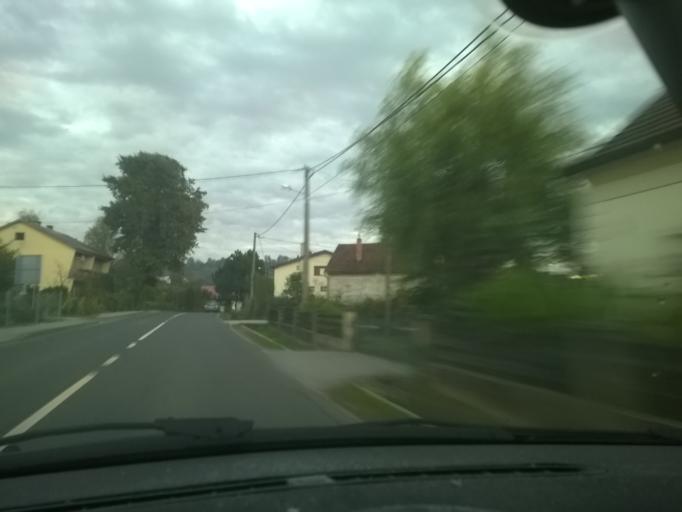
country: HR
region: Krapinsko-Zagorska
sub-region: Grad Krapina
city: Krapina
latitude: 46.1283
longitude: 15.8900
